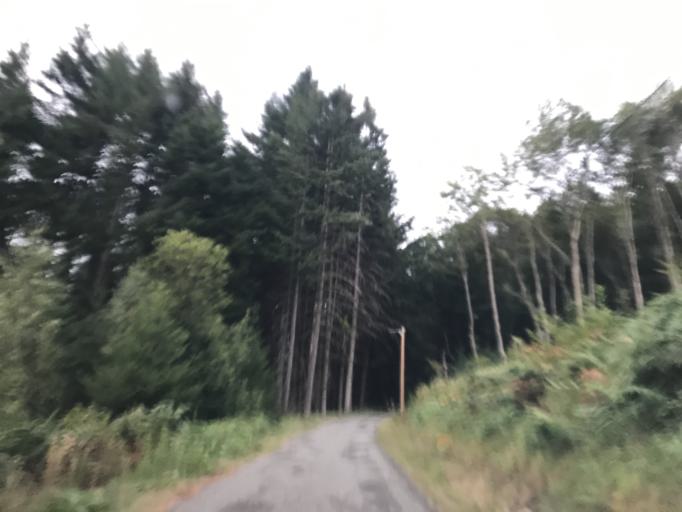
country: FR
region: Auvergne
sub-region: Departement du Puy-de-Dome
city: La Monnerie-le-Montel
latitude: 45.8481
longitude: 3.5892
